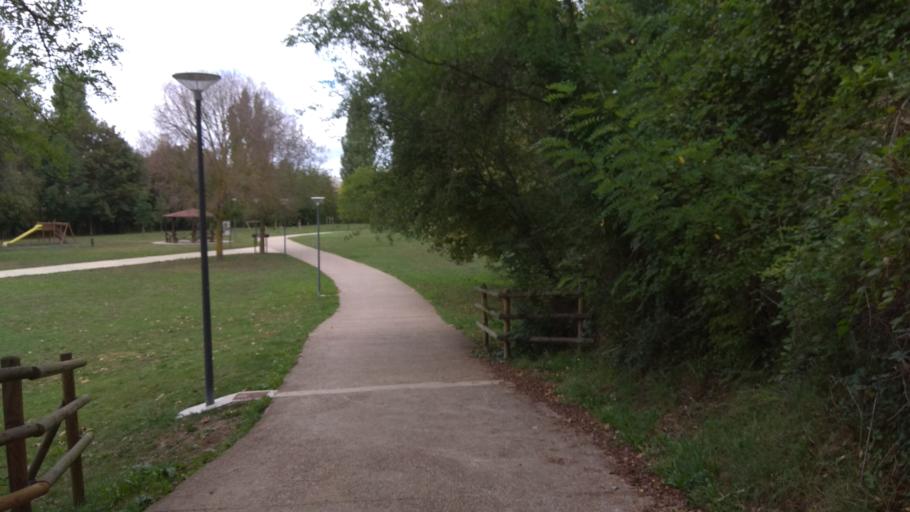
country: ES
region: Navarre
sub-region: Provincia de Navarra
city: Baranain
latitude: 42.8063
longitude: -1.6944
